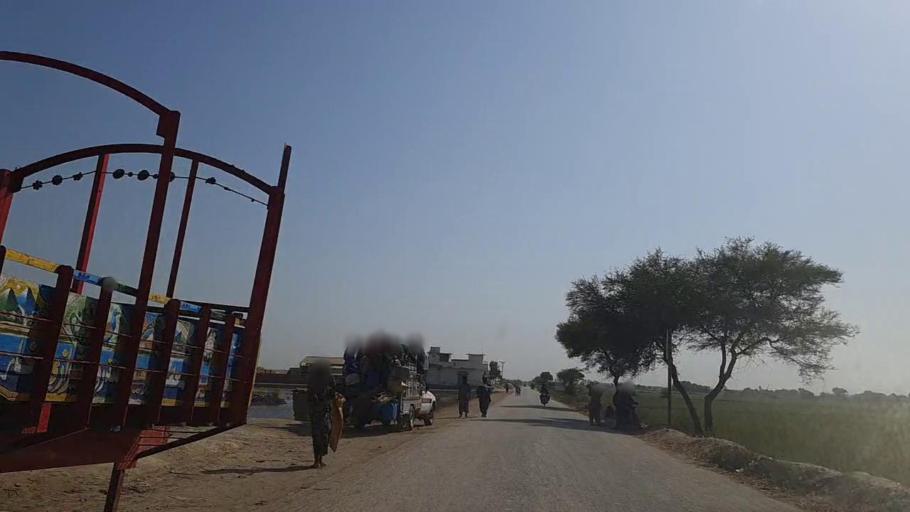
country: PK
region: Sindh
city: Mirpur Batoro
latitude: 24.6153
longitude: 68.2956
